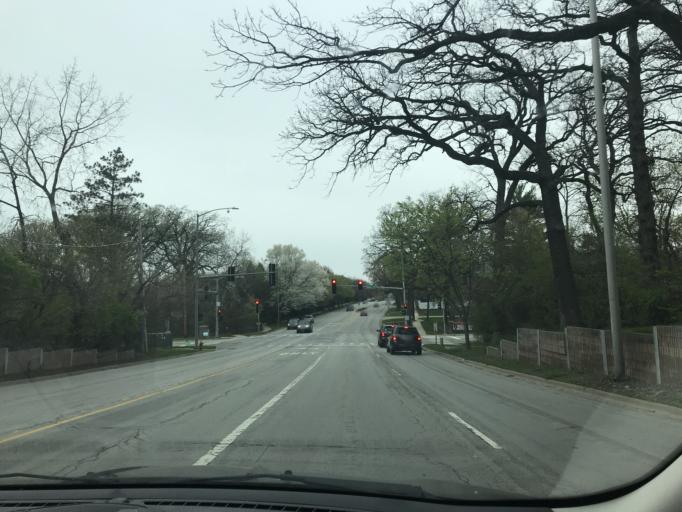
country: US
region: Illinois
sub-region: DuPage County
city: Naperville
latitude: 41.7398
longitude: -88.1179
